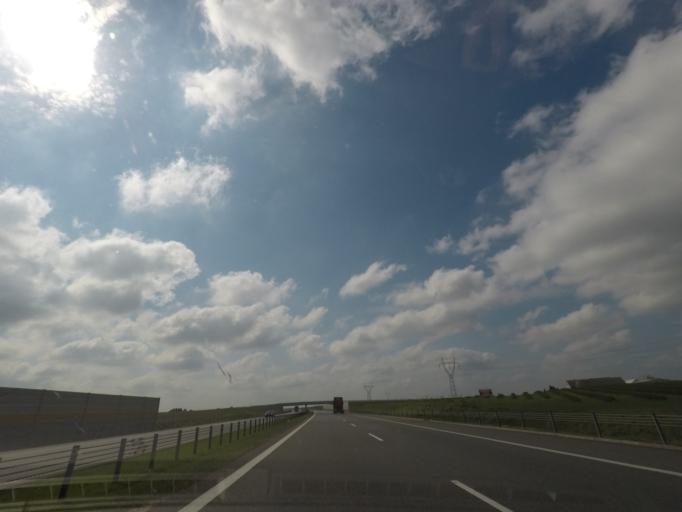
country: PL
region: Kujawsko-Pomorskie
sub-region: Powiat chelminski
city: Lisewo
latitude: 53.2334
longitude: 18.7261
